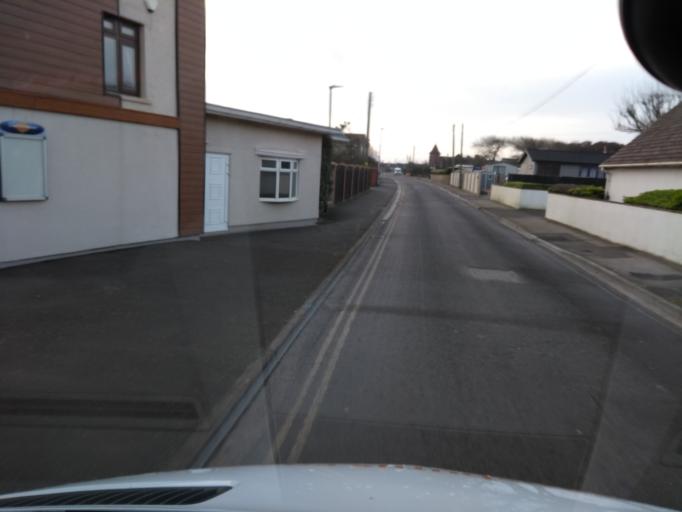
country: GB
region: England
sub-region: North Somerset
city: Weston-super-Mare
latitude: 51.3017
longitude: -3.0100
